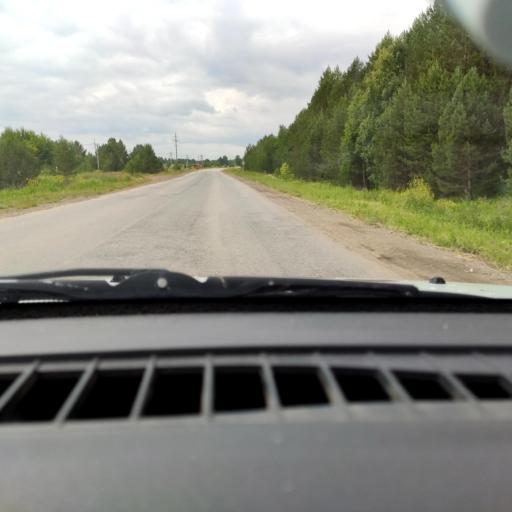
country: RU
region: Perm
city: Orda
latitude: 57.1474
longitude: 56.7563
